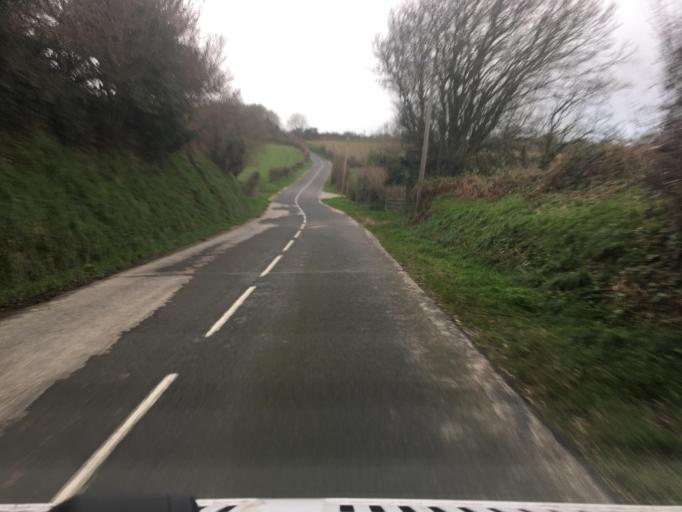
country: FR
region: Lower Normandy
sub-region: Departement de la Manche
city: Beaumont-Hague
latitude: 49.6816
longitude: -1.8524
